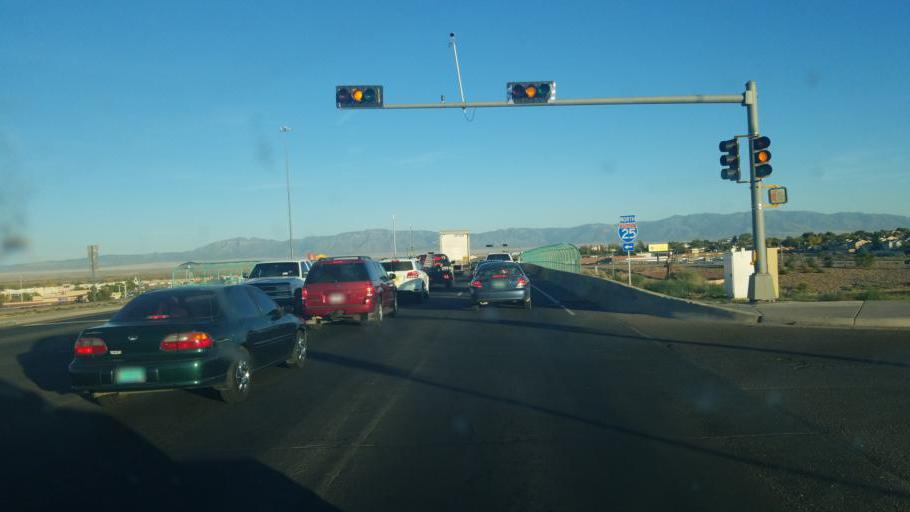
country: US
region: New Mexico
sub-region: Valencia County
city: Los Lunas
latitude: 34.8147
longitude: -106.7622
